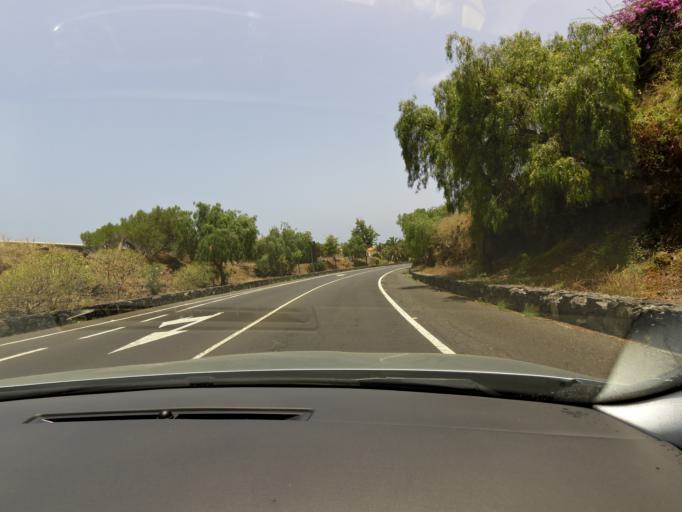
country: ES
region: Canary Islands
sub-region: Provincia de Santa Cruz de Tenerife
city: Puerto de la Cruz
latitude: 28.4092
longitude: -16.5328
